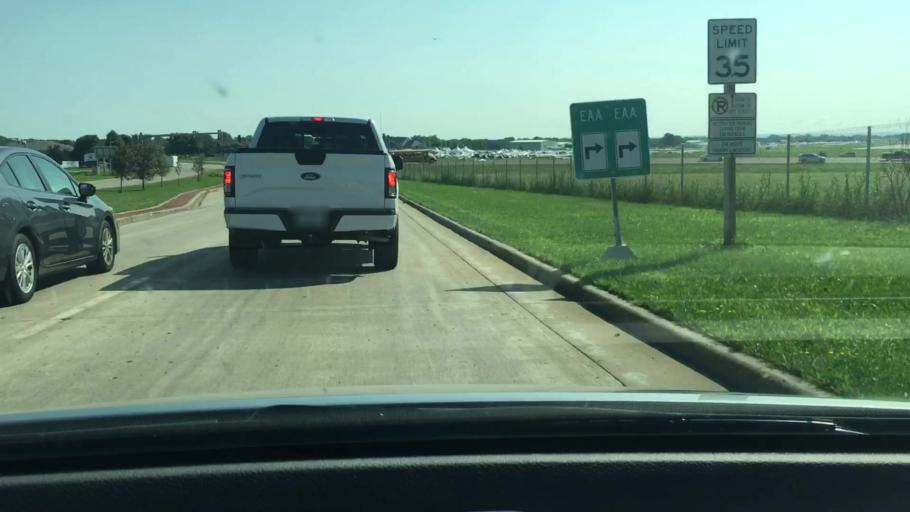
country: US
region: Wisconsin
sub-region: Winnebago County
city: Oshkosh
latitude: 43.9906
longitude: -88.5795
